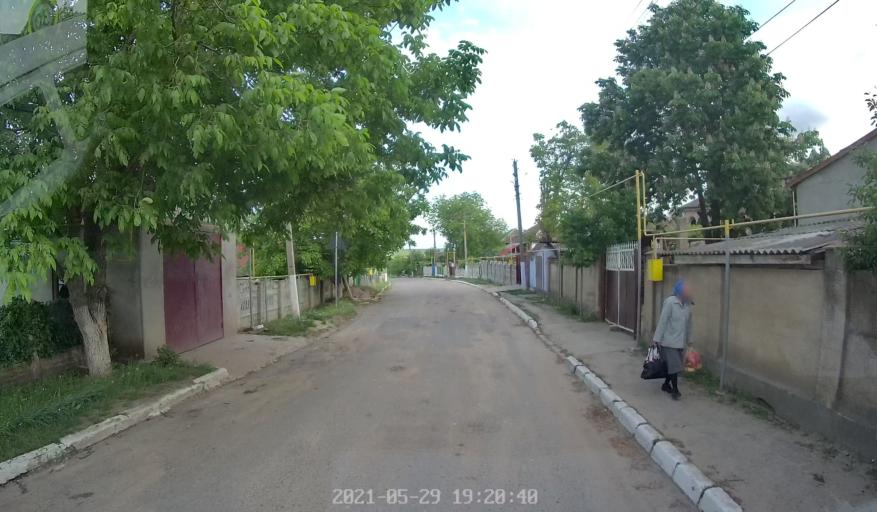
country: MD
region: Chisinau
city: Singera
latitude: 46.8398
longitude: 28.9534
